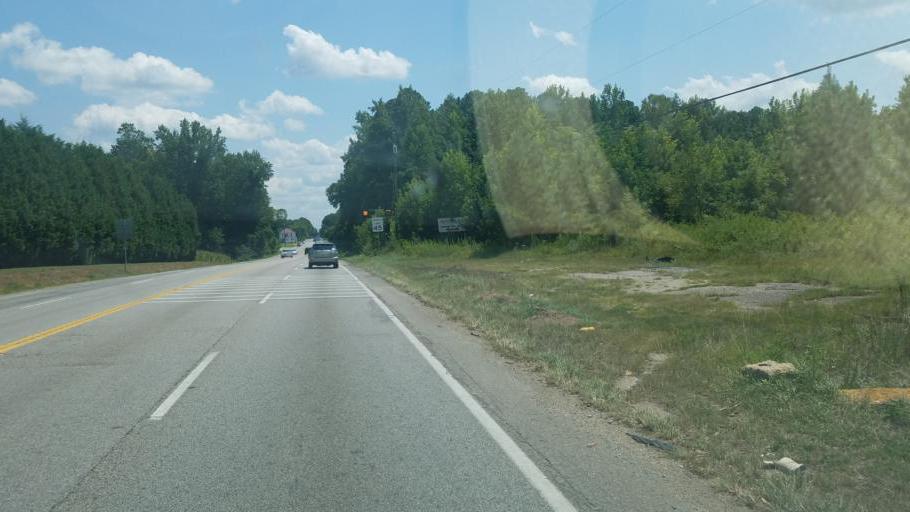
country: US
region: Virginia
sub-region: Prince George County
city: Prince George
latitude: 37.1291
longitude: -77.2340
